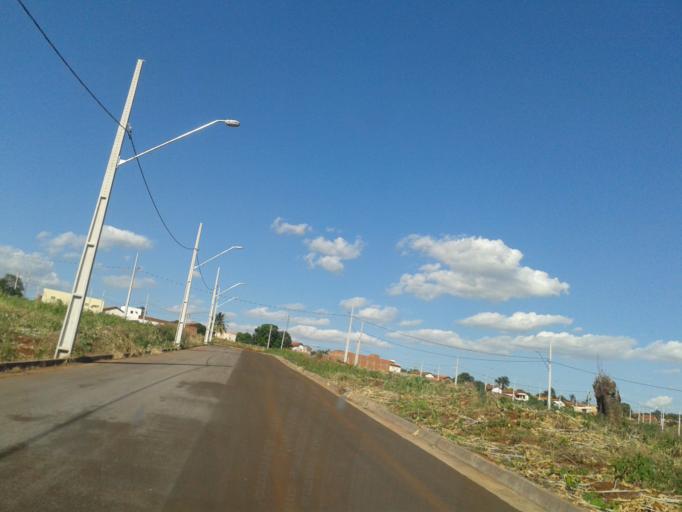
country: BR
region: Minas Gerais
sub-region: Capinopolis
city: Capinopolis
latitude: -18.6878
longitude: -49.5715
